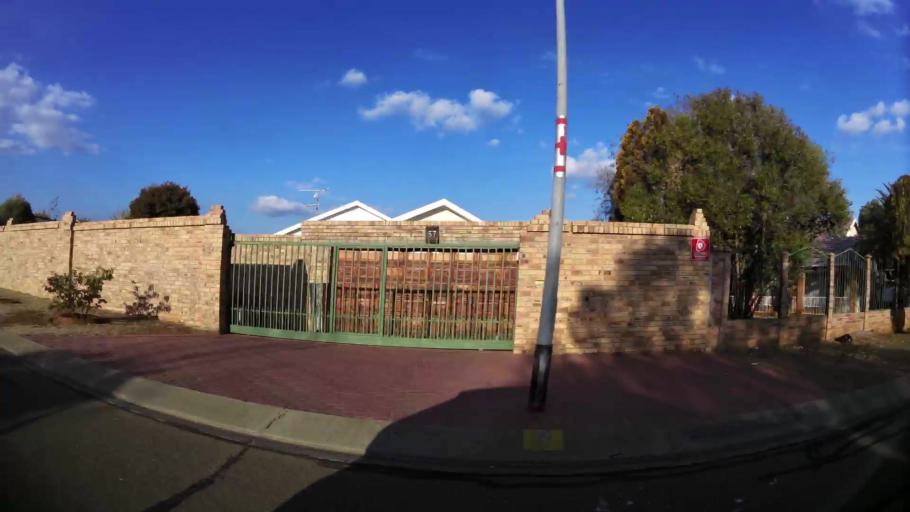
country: ZA
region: Orange Free State
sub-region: Mangaung Metropolitan Municipality
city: Bloemfontein
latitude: -29.1572
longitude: 26.1827
